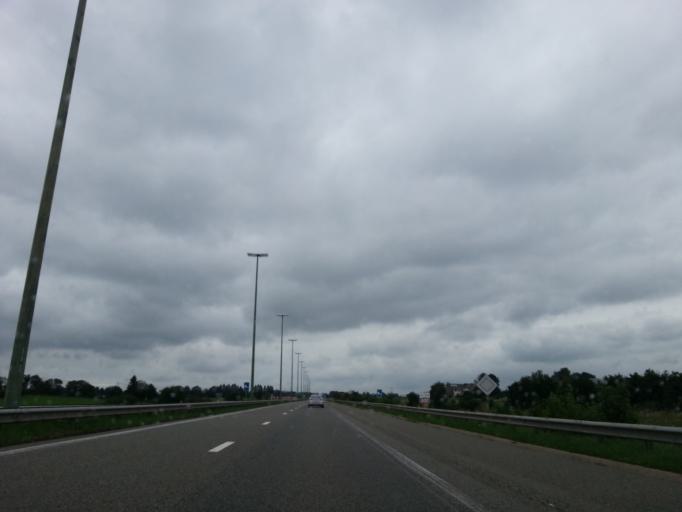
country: BE
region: Wallonia
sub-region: Province de Liege
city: Saint-Vith
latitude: 50.2734
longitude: 6.1102
